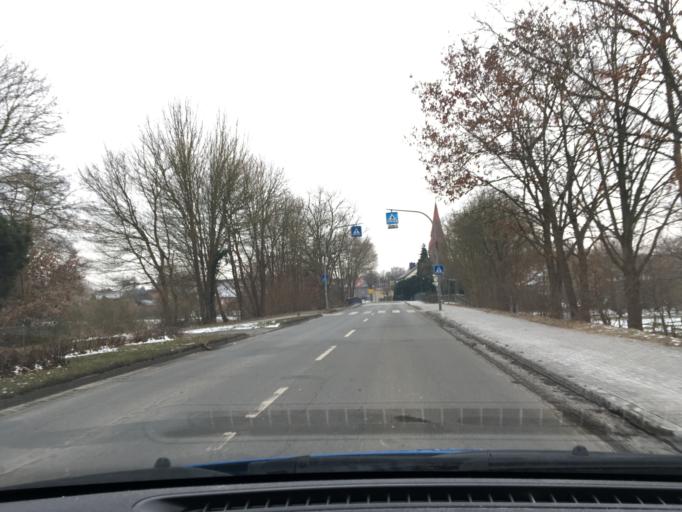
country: DE
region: Lower Saxony
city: Bienenbuttel
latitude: 53.1441
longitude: 10.4911
